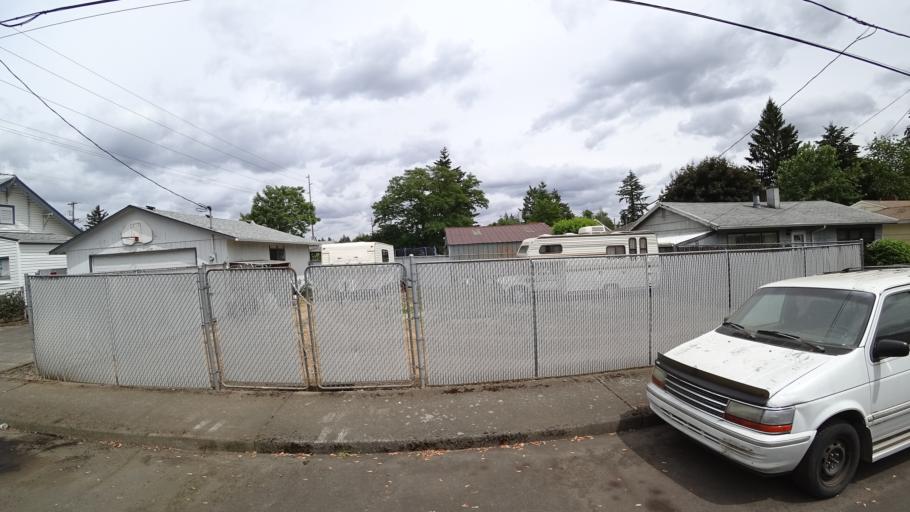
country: US
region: Oregon
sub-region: Multnomah County
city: Lents
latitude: 45.4895
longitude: -122.5596
